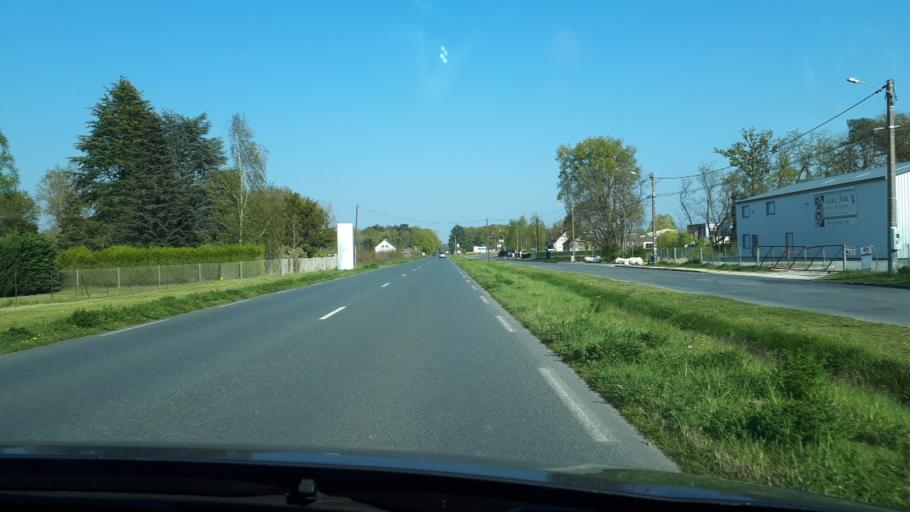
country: FR
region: Centre
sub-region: Departement d'Indre-et-Loire
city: Civray-de-Touraine
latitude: 47.3233
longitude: 1.0223
